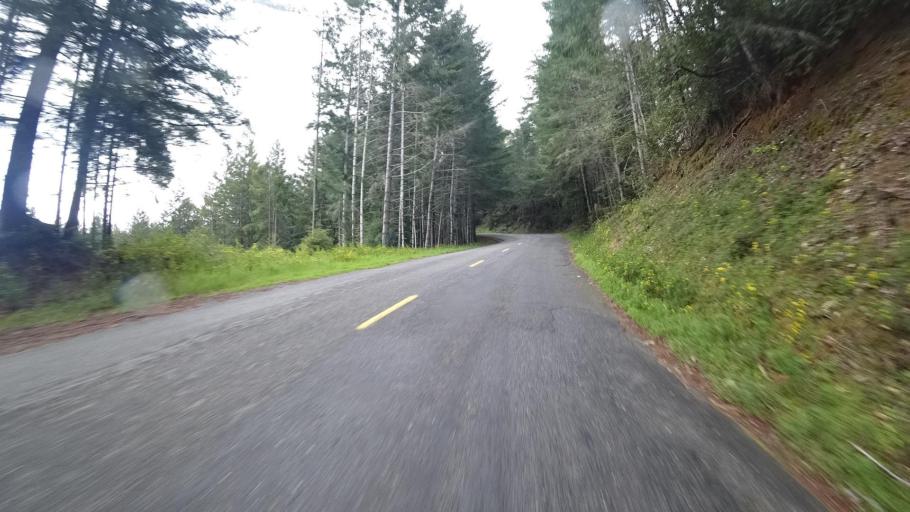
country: US
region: California
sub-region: Humboldt County
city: Redway
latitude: 40.2786
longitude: -123.7940
